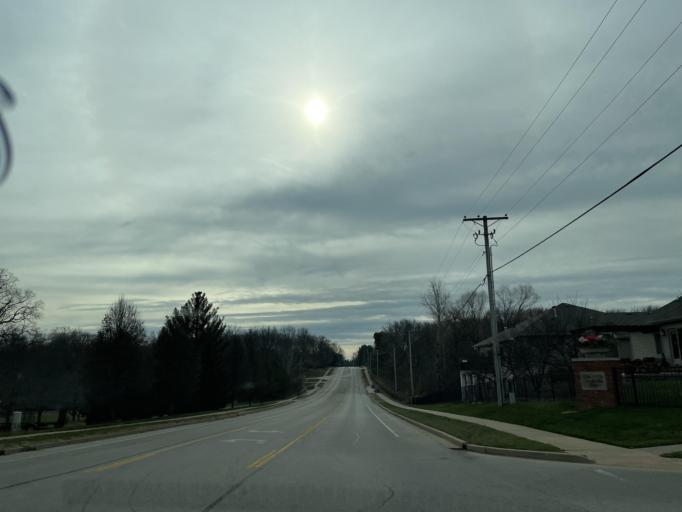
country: US
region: Illinois
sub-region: Sangamon County
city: Leland Grove
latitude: 39.7949
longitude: -89.7298
